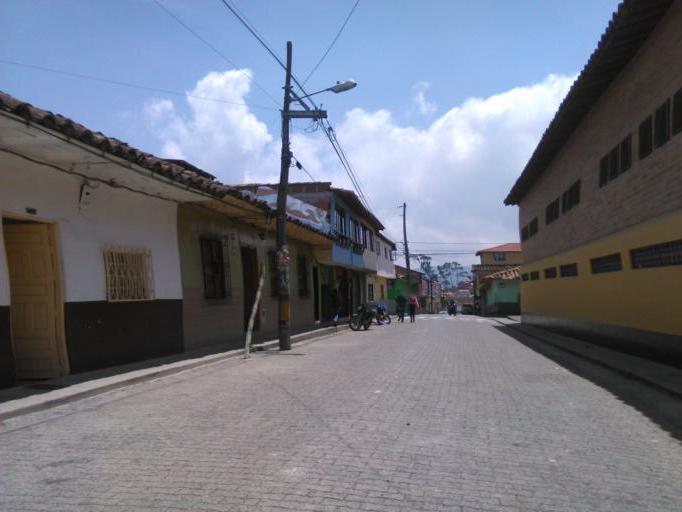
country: CO
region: Antioquia
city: La Union
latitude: 5.9722
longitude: -75.3616
